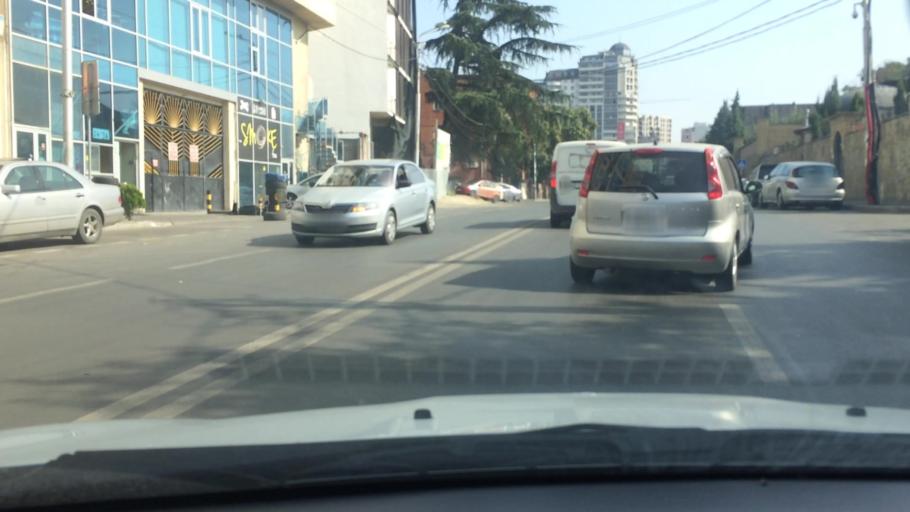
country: GE
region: T'bilisi
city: Tbilisi
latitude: 41.6868
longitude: 44.8266
